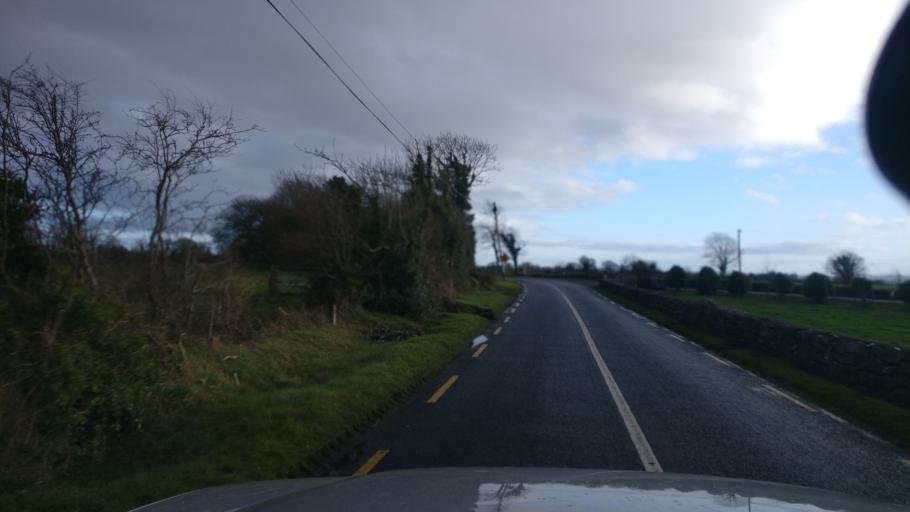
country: IE
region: Connaught
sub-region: County Galway
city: Athenry
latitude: 53.2935
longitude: -8.6472
